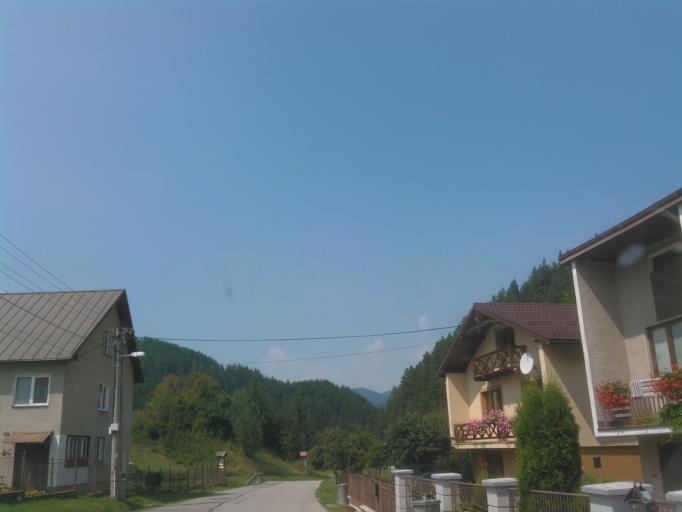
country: SK
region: Zilinsky
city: Ruzomberok
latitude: 48.9400
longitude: 19.2987
